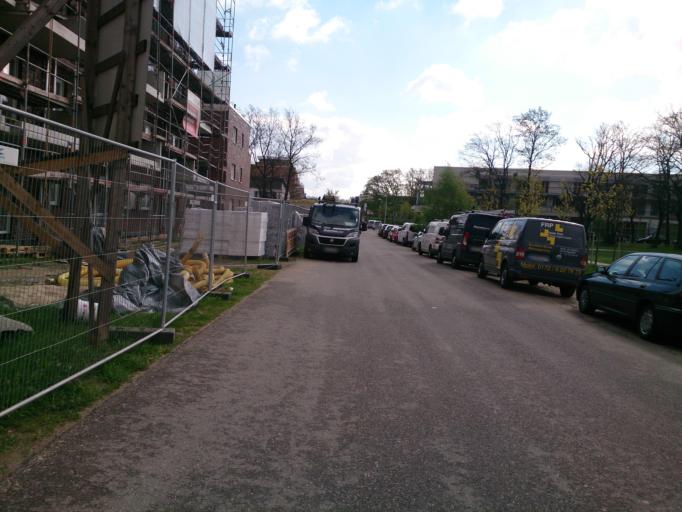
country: DE
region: Lower Saxony
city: Neu Wulmstorf
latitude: 53.4762
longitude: 9.8524
